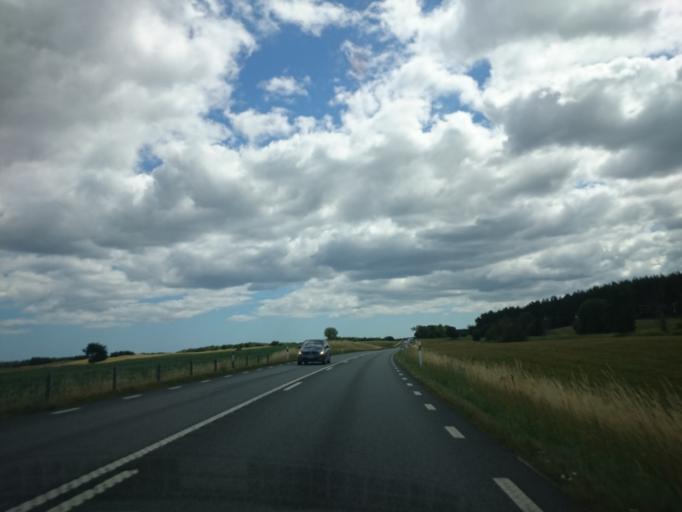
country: SE
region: Skane
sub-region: Kristianstads Kommun
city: Degeberga
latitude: 55.8231
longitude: 14.1133
